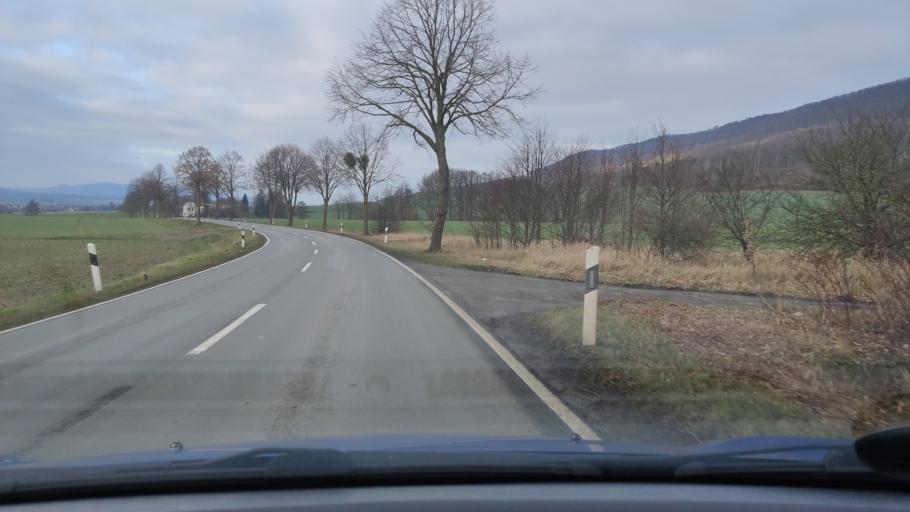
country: DE
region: Lower Saxony
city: Heyen
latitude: 52.0633
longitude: 9.5242
